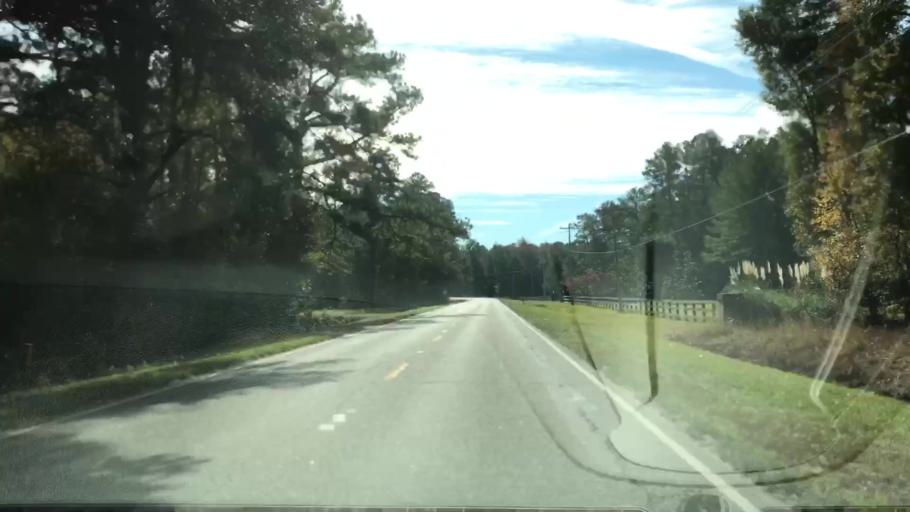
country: US
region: South Carolina
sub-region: Colleton County
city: Walterboro
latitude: 32.8681
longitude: -80.6125
